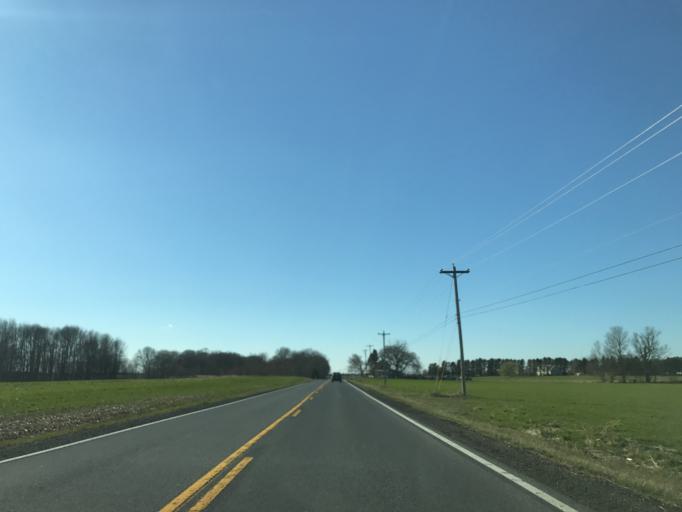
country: US
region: Maryland
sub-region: Queen Anne's County
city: Centreville
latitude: 39.0041
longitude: -75.9741
